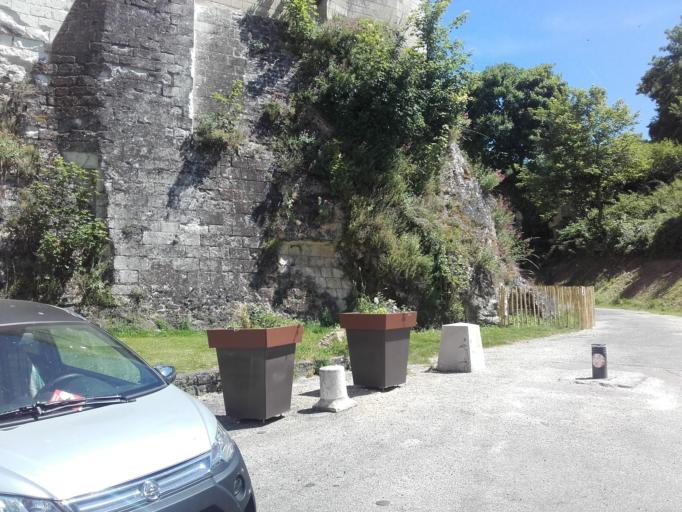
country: FR
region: Centre
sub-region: Departement d'Indre-et-Loire
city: Loches
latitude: 47.1247
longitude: 0.9961
